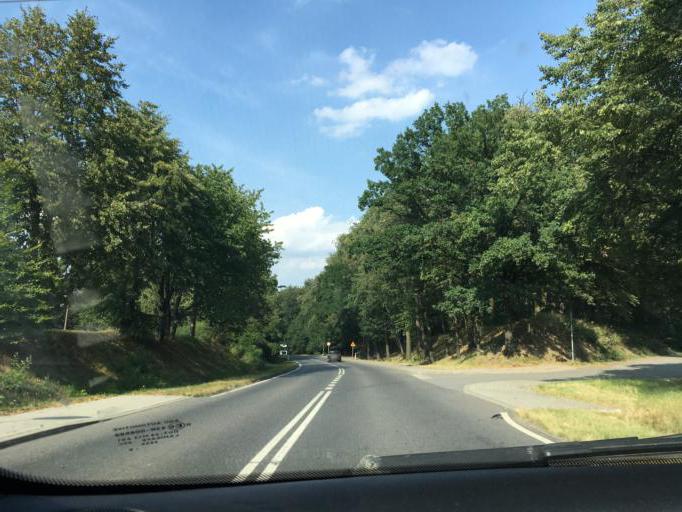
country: PL
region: Opole Voivodeship
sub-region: Powiat prudnicki
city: Laka Prudnicka
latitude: 50.4015
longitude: 17.5089
